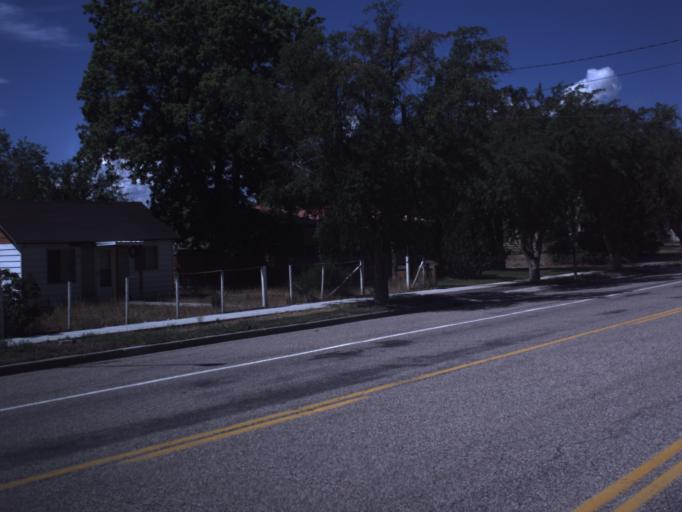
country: US
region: Utah
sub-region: Piute County
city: Junction
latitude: 38.1718
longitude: -112.2731
